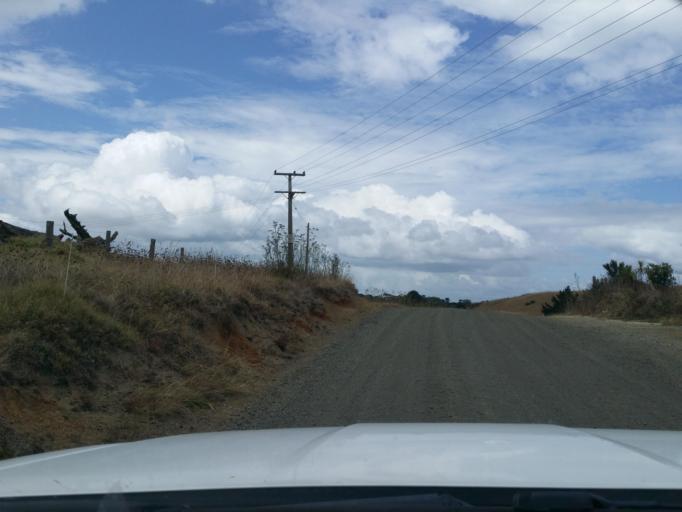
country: NZ
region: Auckland
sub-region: Auckland
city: Wellsford
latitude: -36.3467
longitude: 174.1686
